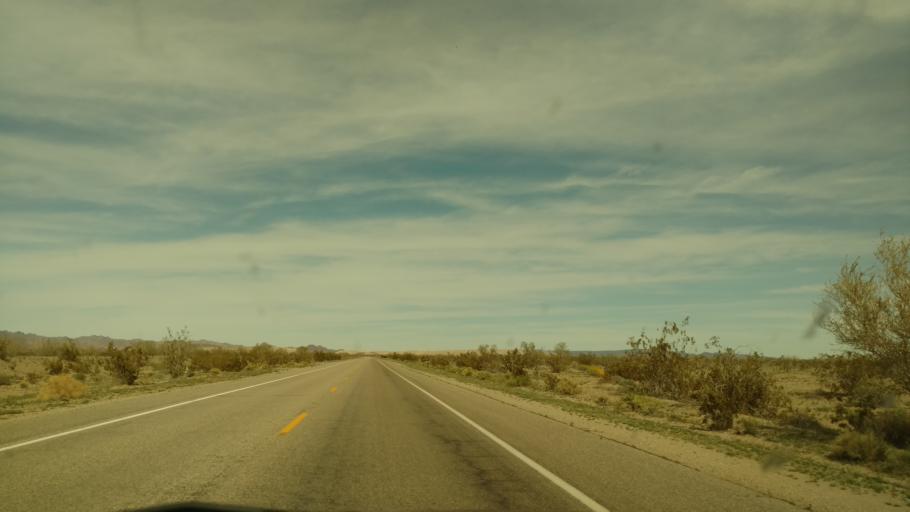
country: US
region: California
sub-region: Imperial County
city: Holtville
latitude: 33.0036
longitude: -115.0618
